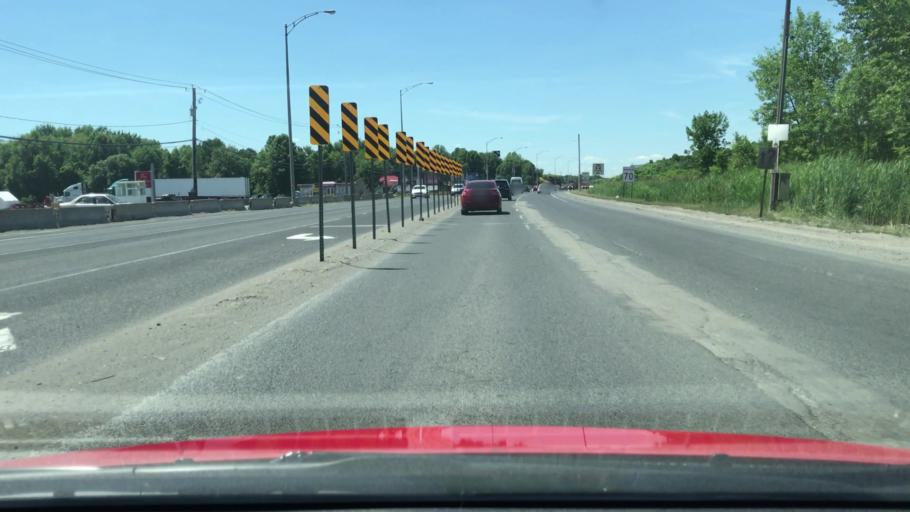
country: CA
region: Quebec
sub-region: Monteregie
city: Saint-Constant
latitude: 45.3955
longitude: -73.6077
